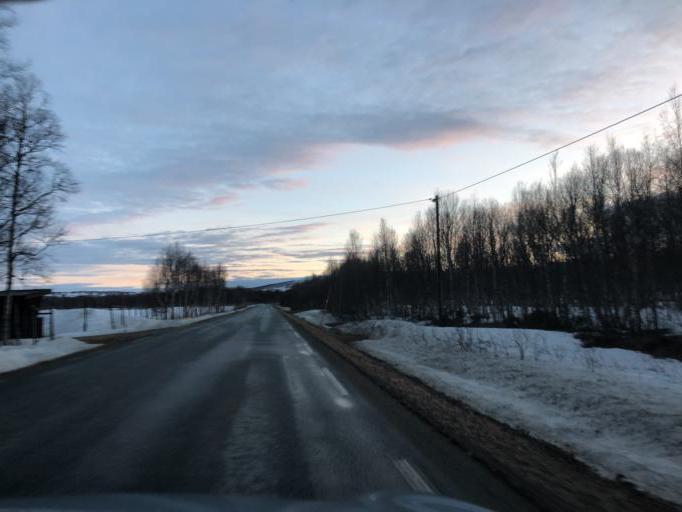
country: NO
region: Sor-Trondelag
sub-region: Tydal
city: Aas
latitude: 62.6746
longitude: 11.8352
